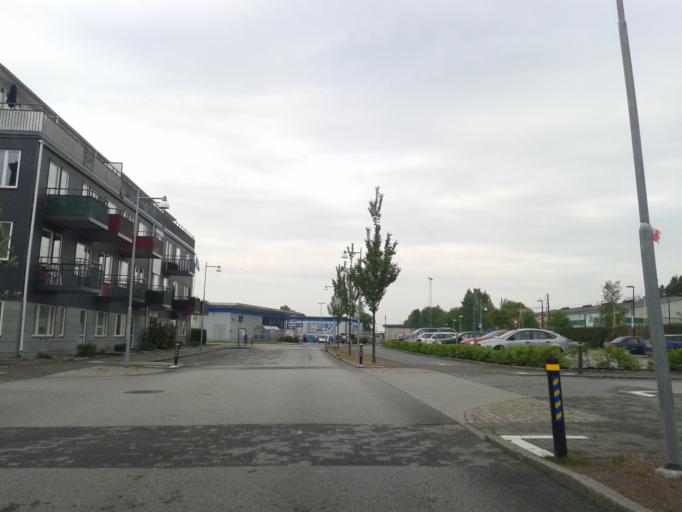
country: SE
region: Vaestra Goetaland
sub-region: Kungalvs Kommun
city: Kungalv
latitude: 57.8605
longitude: 11.9176
